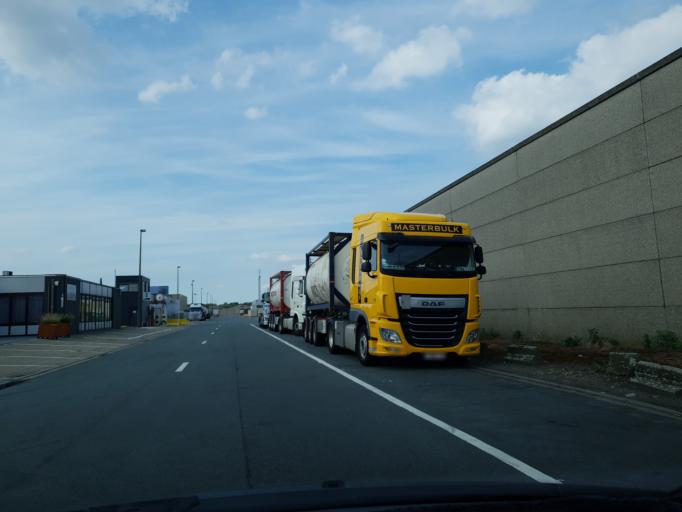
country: BE
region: Flanders
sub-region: Provincie Antwerpen
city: Antwerpen
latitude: 51.2694
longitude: 4.3958
